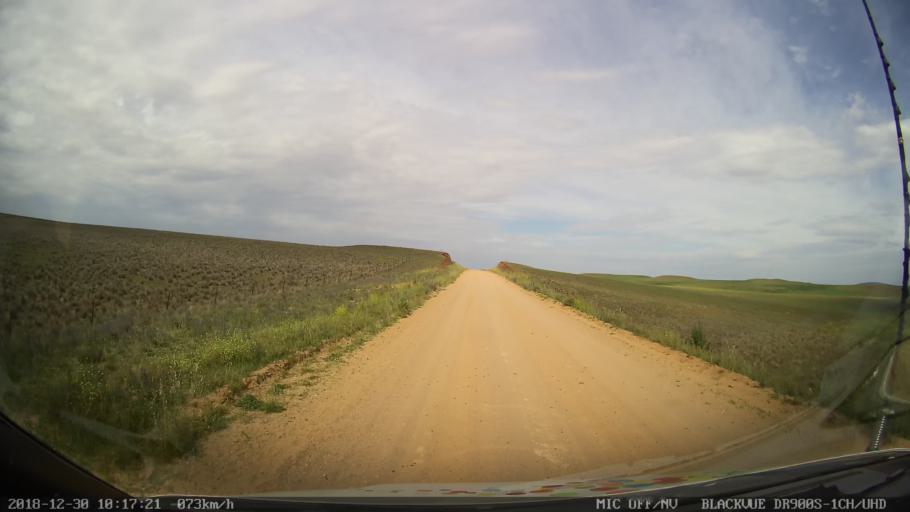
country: AU
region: New South Wales
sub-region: Snowy River
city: Berridale
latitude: -36.5481
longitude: 149.0221
